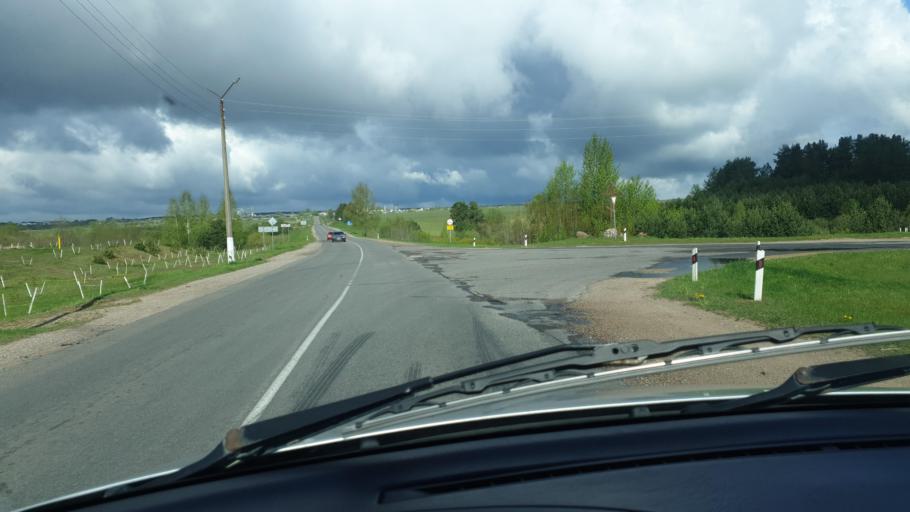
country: BY
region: Vitebsk
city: Lyepyel'
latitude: 54.8826
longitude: 28.6553
